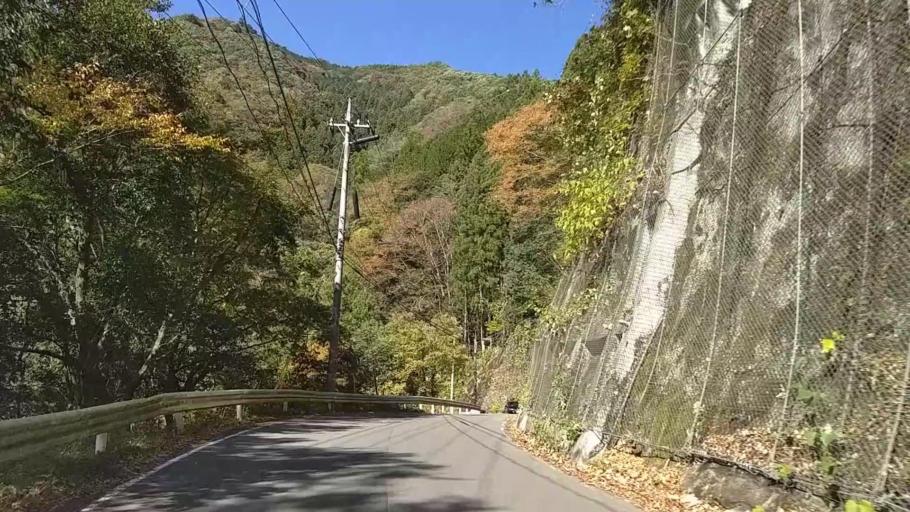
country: JP
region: Yamanashi
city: Uenohara
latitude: 35.6833
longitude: 139.0577
